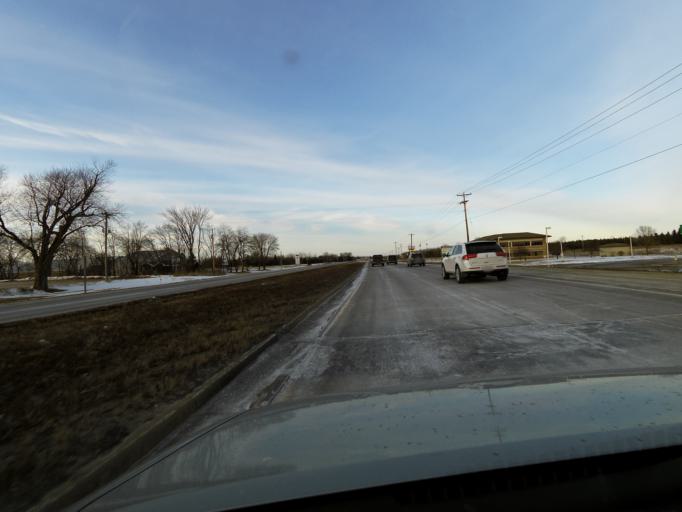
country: US
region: Wisconsin
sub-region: Saint Croix County
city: Hudson
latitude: 44.9685
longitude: -92.6799
